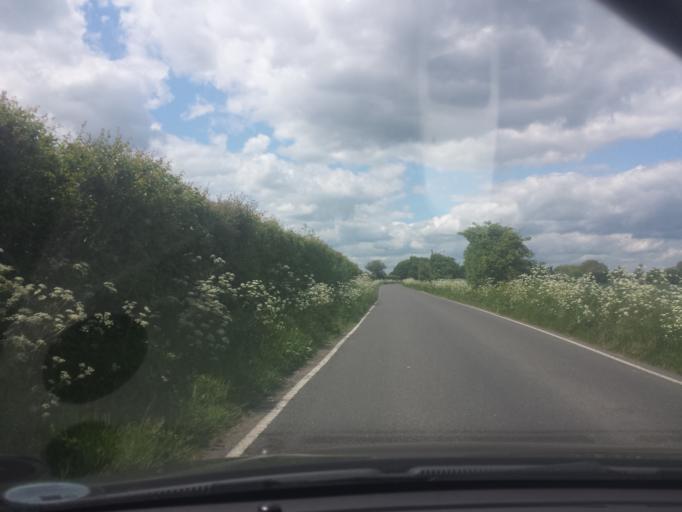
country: GB
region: England
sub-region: Essex
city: Little Clacton
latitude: 51.8880
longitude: 1.1567
